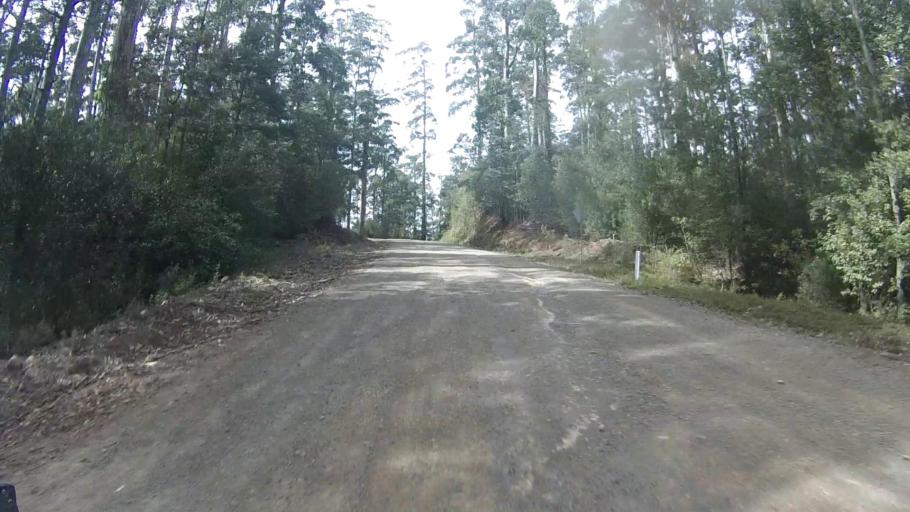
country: AU
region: Tasmania
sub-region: Sorell
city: Sorell
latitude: -42.7033
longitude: 147.8562
